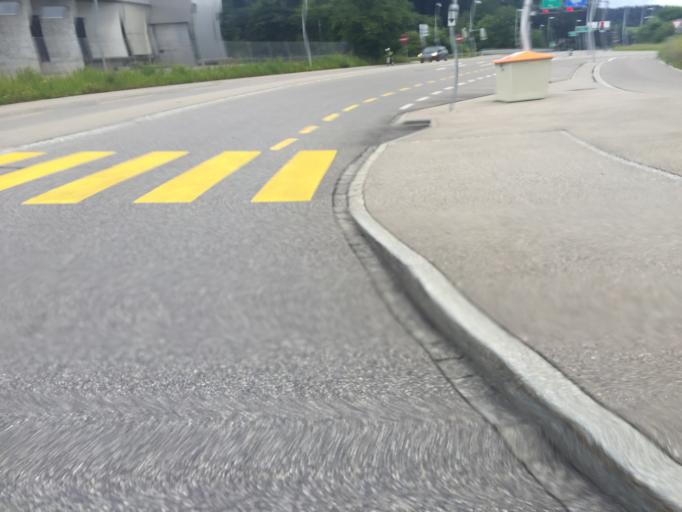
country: CH
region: Bern
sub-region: Bern-Mittelland District
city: Wohlen
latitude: 46.9431
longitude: 7.3701
